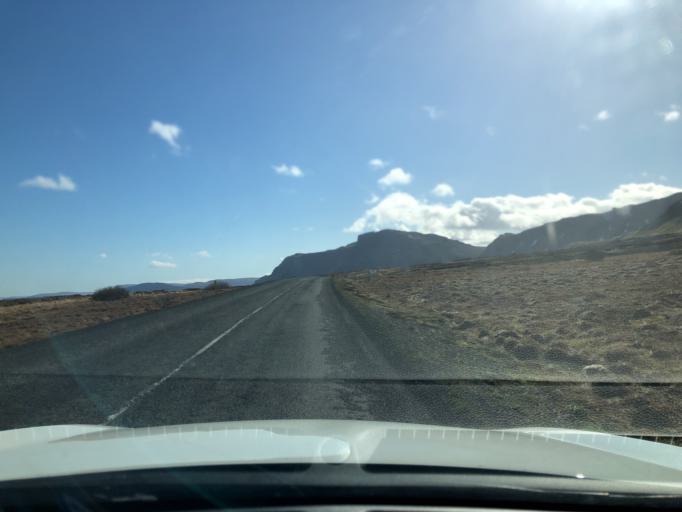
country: IS
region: West
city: Borgarnes
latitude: 64.5245
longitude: -21.8577
